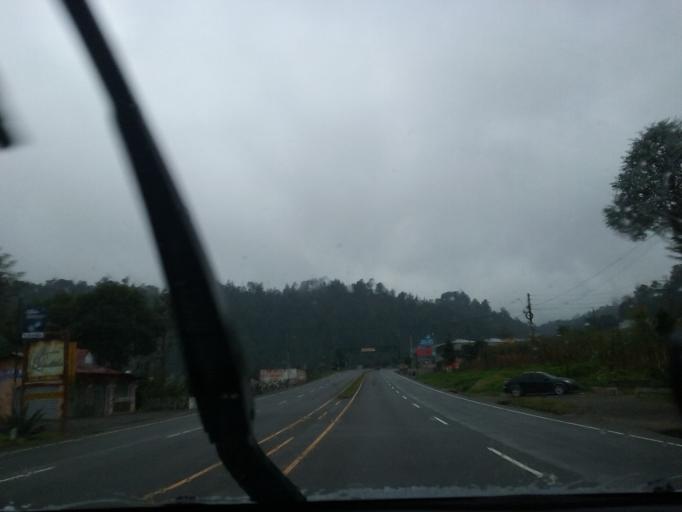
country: GT
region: Solola
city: Santa Lucia Utatlan
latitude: 14.7972
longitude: -91.2526
